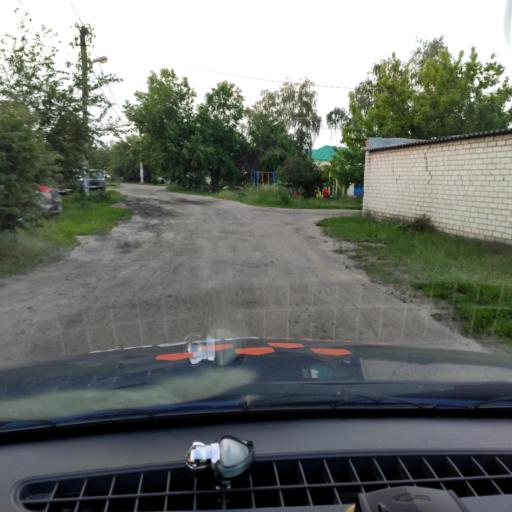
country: RU
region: Voronezj
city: Somovo
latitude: 51.7470
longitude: 39.3456
